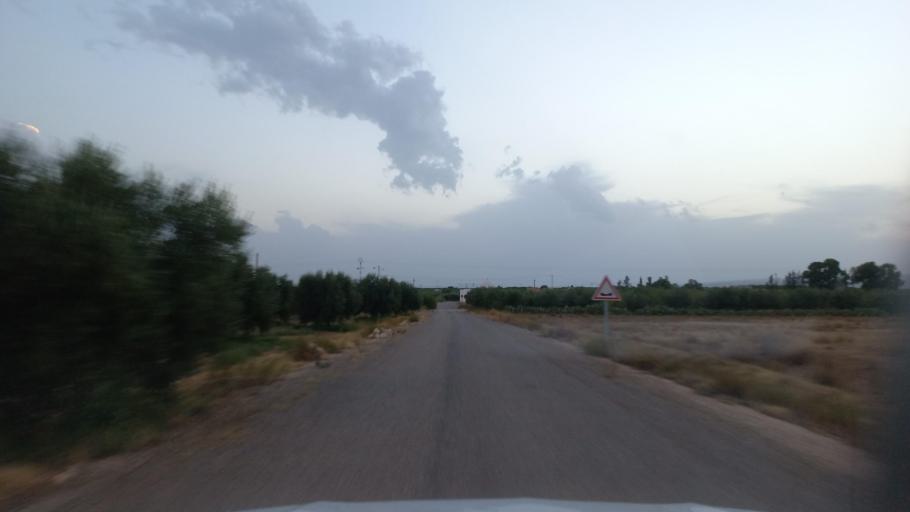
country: TN
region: Al Qasrayn
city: Kasserine
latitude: 35.2738
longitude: 9.0388
